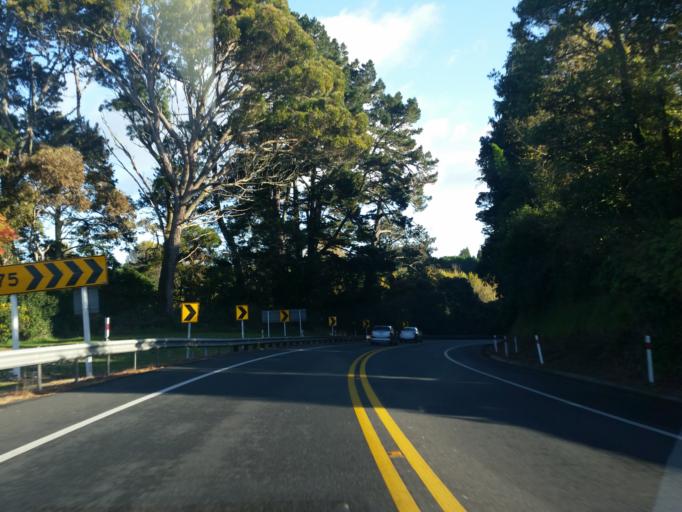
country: NZ
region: Bay of Plenty
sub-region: Tauranga City
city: Tauranga
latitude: -37.7001
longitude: 176.0787
